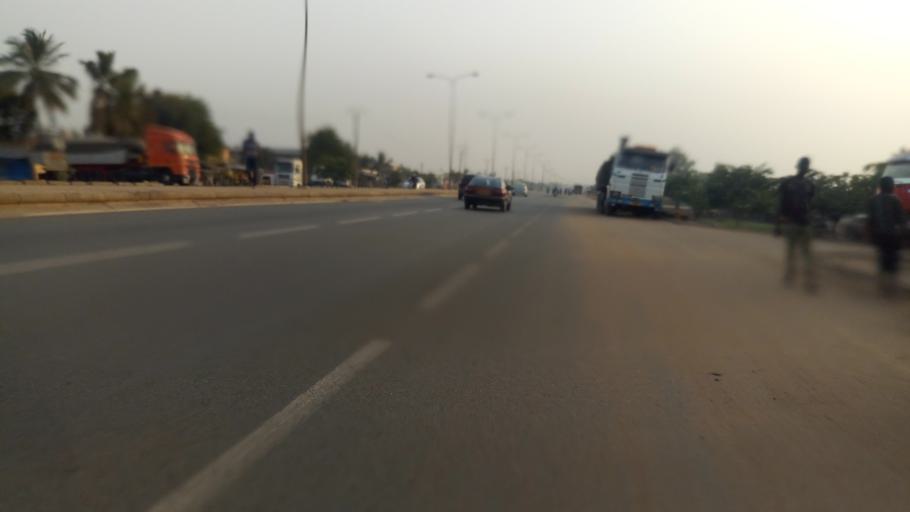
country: TG
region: Maritime
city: Lome
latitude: 6.2727
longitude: 1.2103
